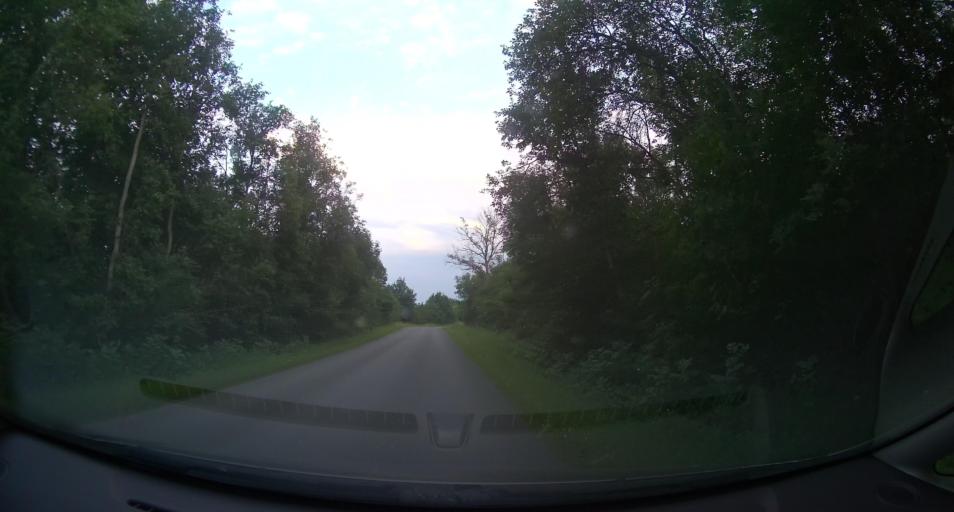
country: EE
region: Laeaene
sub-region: Lihula vald
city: Lihula
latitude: 58.5903
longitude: 23.6118
